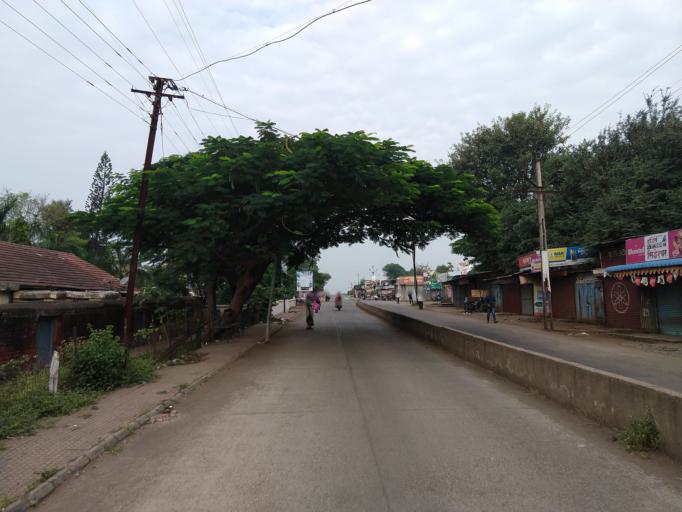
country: IN
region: Maharashtra
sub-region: Pune Division
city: Sasvad
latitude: 18.3465
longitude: 74.0273
